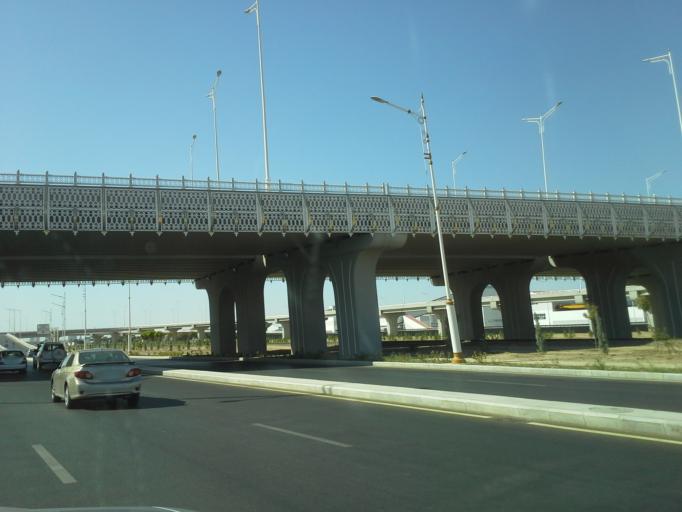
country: TM
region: Ahal
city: Ashgabat
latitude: 37.9270
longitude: 58.4281
